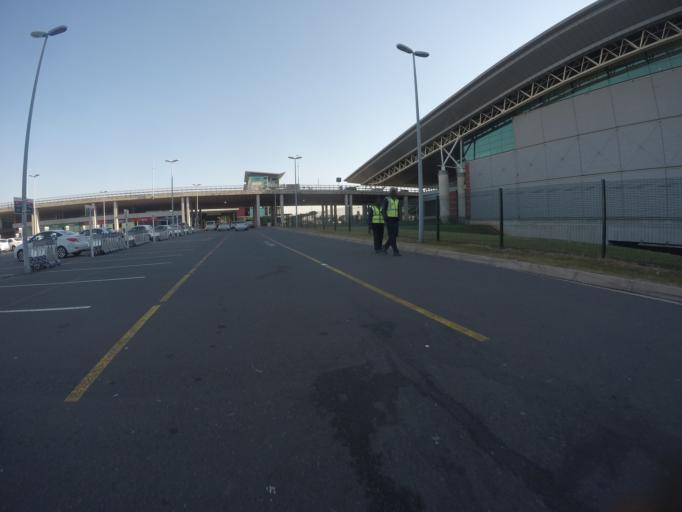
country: ZA
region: KwaZulu-Natal
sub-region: iLembe District Municipality
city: Ballitoville
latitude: -29.6199
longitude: 31.1042
